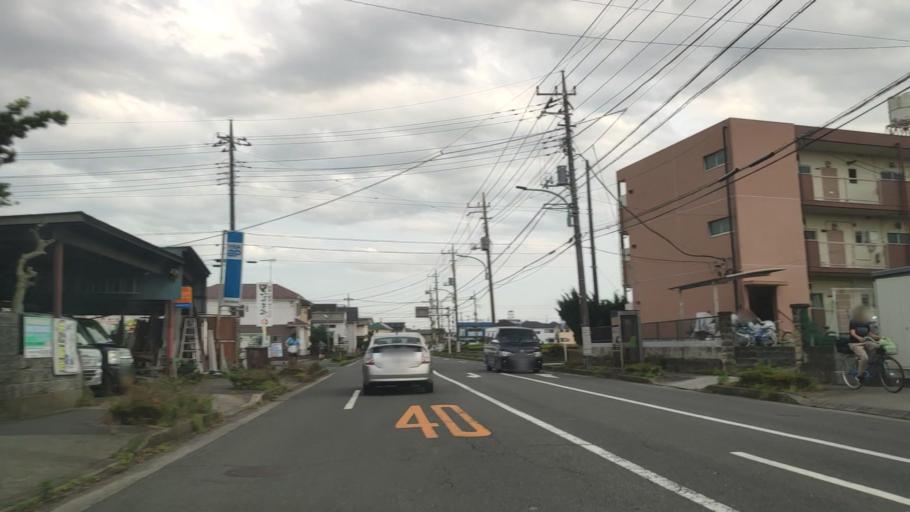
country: JP
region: Tokyo
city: Ome
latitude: 35.7964
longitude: 139.2982
